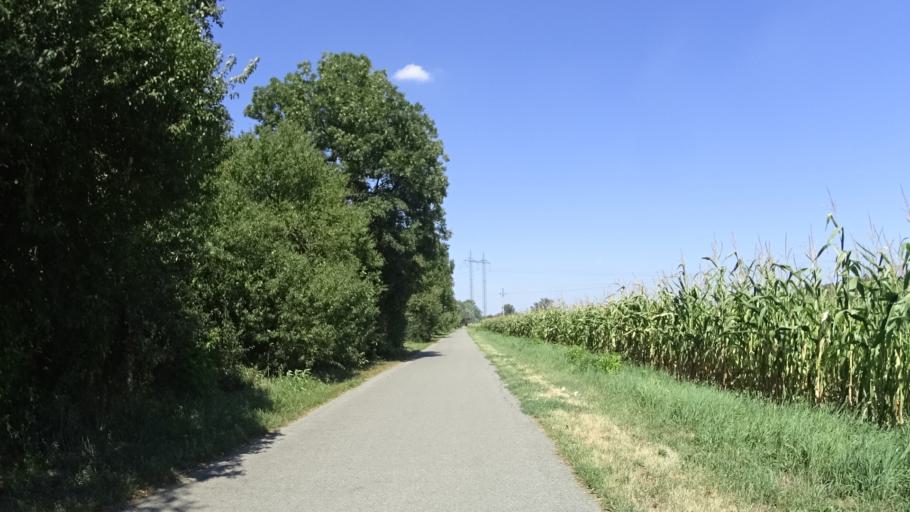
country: CZ
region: South Moravian
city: Straznice
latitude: 48.9106
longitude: 17.3233
